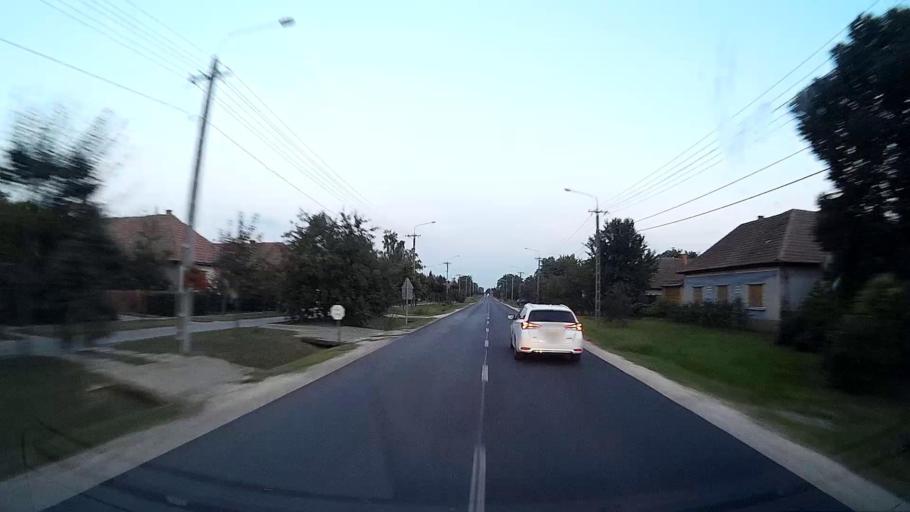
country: HU
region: Pest
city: Cegledbercel
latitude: 47.2267
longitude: 19.6614
